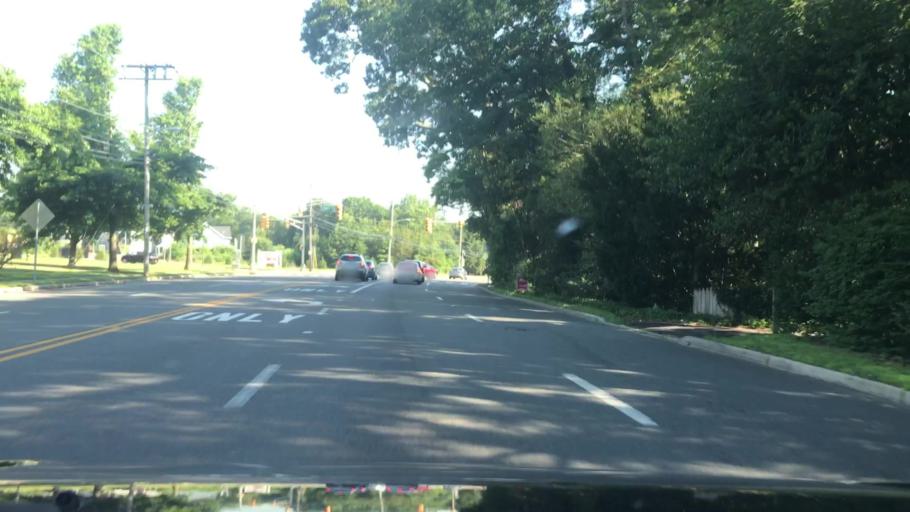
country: US
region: New Jersey
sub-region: Ocean County
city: Leisure Village
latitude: 40.0176
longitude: -74.1986
